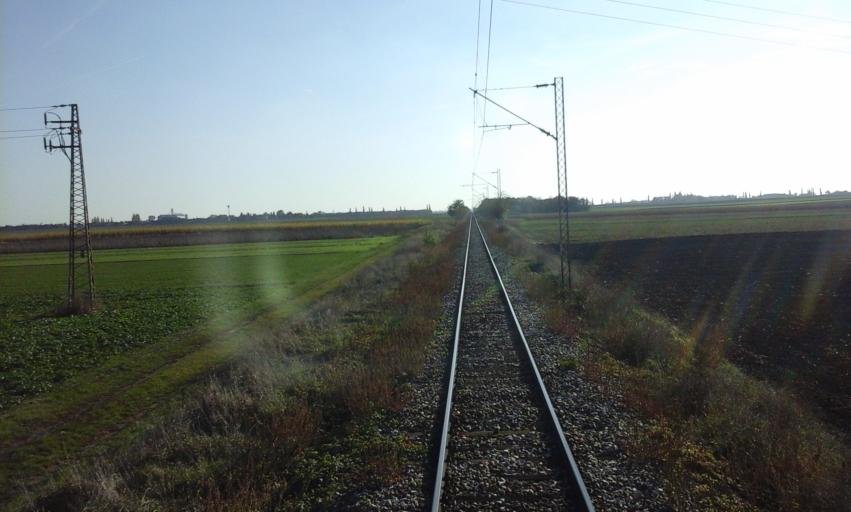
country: RS
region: Autonomna Pokrajina Vojvodina
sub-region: Severnobacki Okrug
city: Backa Topola
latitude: 45.7915
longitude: 19.6475
